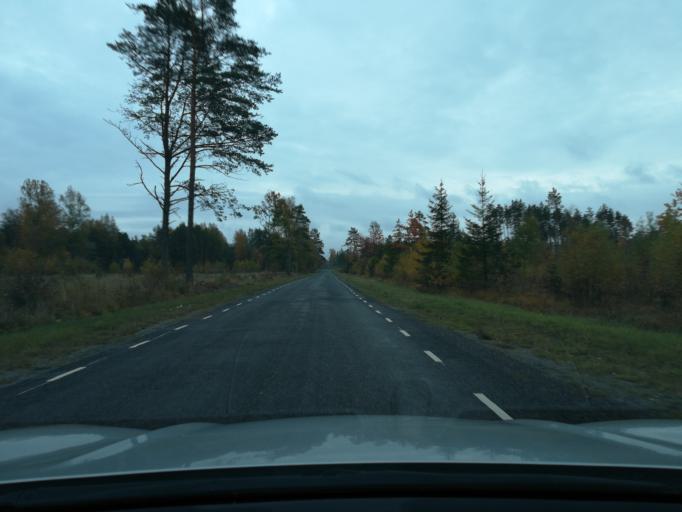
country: EE
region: Ida-Virumaa
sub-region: Johvi vald
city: Johvi
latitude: 59.0241
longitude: 27.3972
